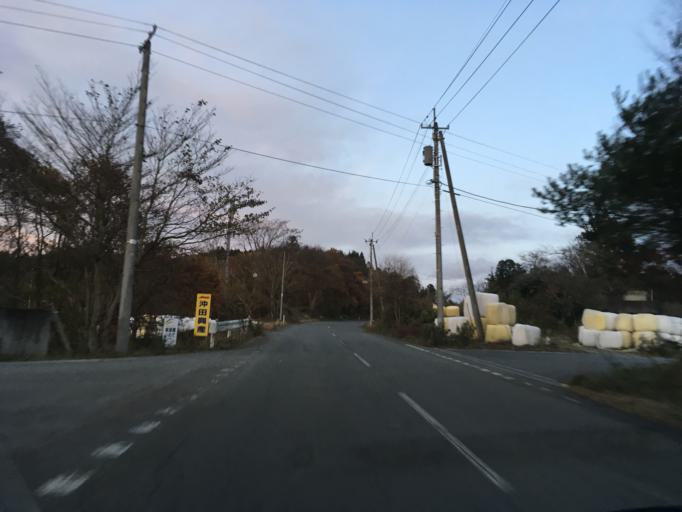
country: JP
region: Iwate
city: Ichinoseki
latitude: 38.7907
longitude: 141.2346
